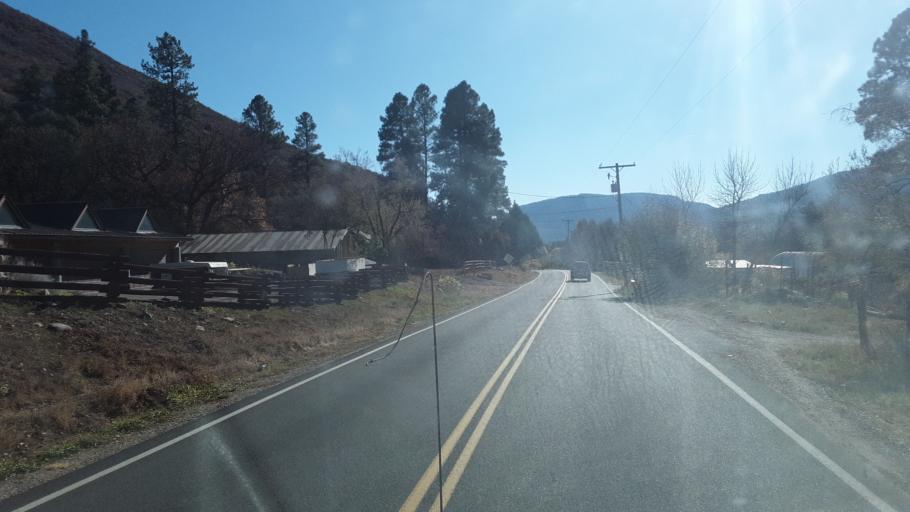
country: US
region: Colorado
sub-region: La Plata County
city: Durango
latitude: 37.3840
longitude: -107.8344
